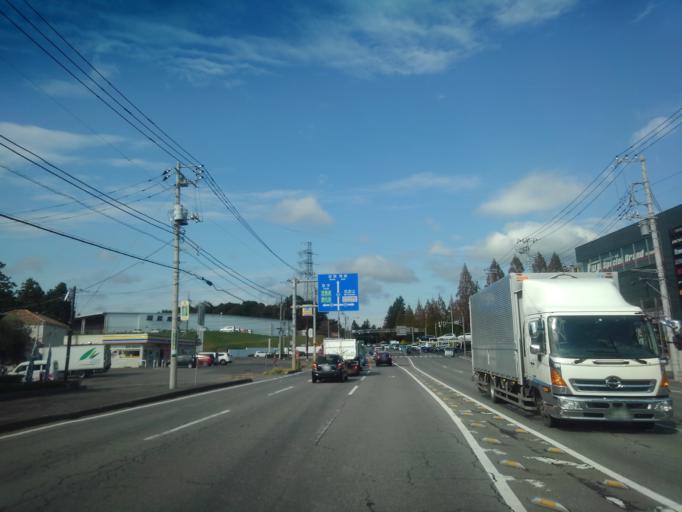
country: JP
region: Ibaraki
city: Naka
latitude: 36.0721
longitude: 140.0858
